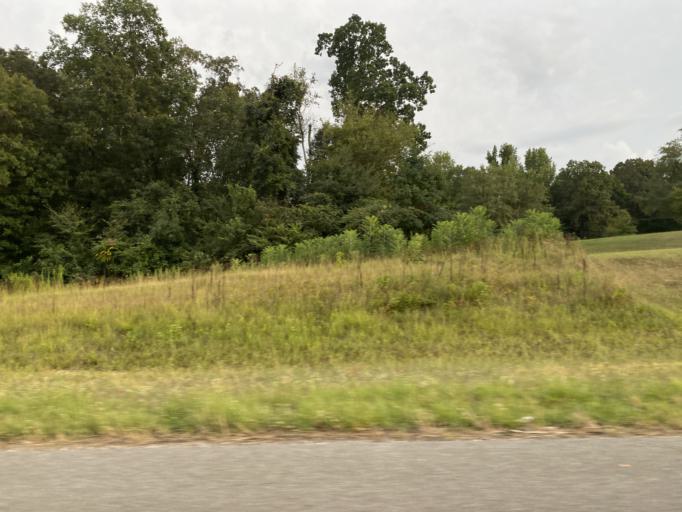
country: US
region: Alabama
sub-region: Franklin County
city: Red Bay
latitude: 34.4492
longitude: -88.0550
